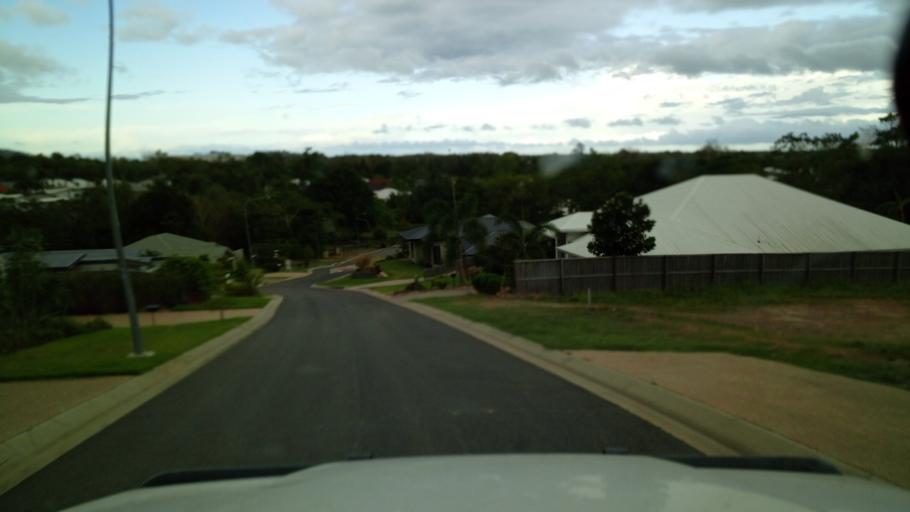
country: AU
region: Queensland
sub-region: Cairns
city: Redlynch
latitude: -16.8440
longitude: 145.6869
